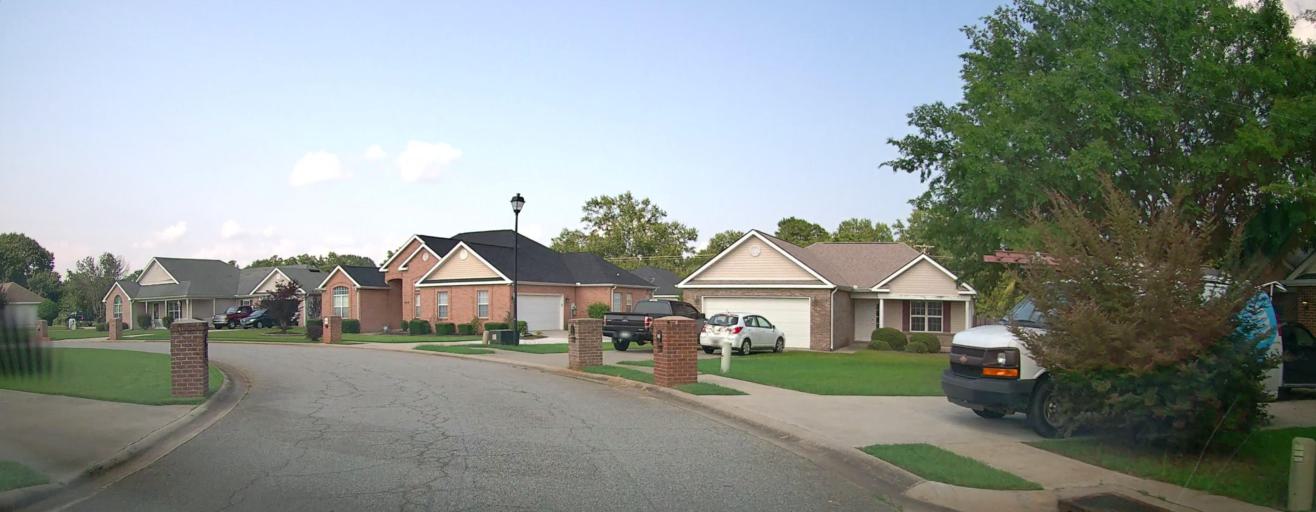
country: US
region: Georgia
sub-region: Houston County
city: Centerville
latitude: 32.6491
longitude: -83.6959
